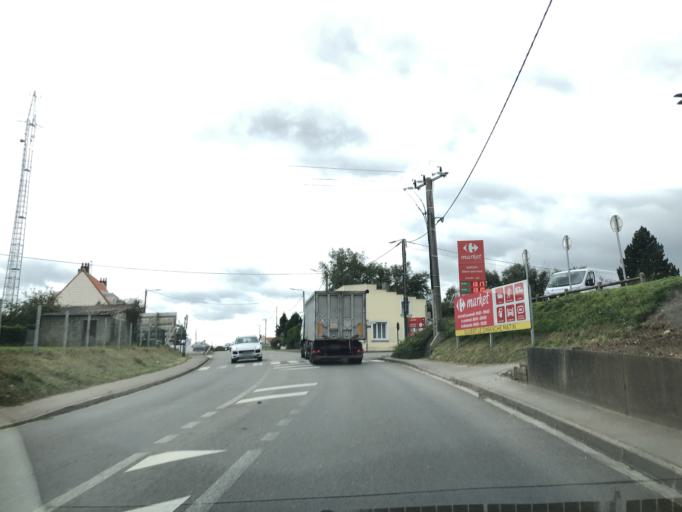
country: FR
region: Nord-Pas-de-Calais
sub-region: Departement du Pas-de-Calais
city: Fruges
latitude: 50.5099
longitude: 2.1325
